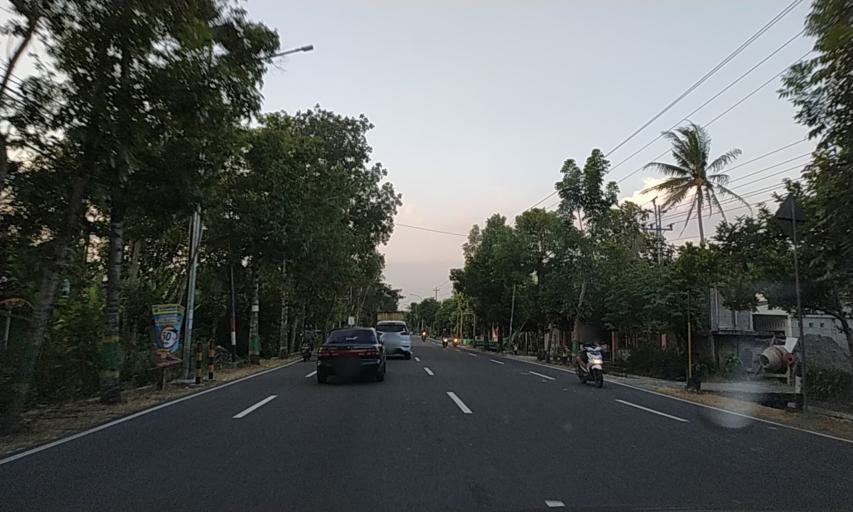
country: ID
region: Daerah Istimewa Yogyakarta
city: Srandakan
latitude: -7.8887
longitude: 110.1300
